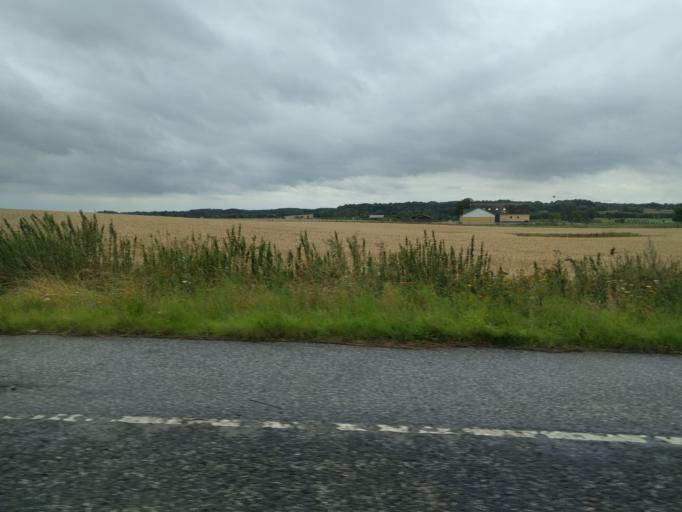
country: DK
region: Zealand
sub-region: Faxe Kommune
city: Ronnede
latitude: 55.2579
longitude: 12.0137
